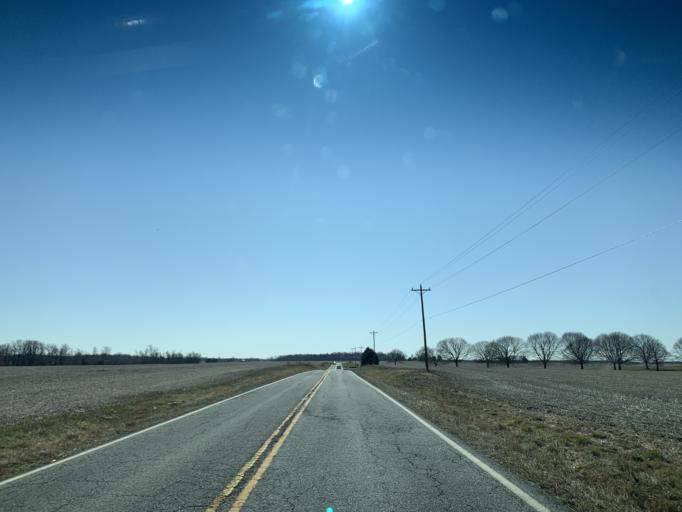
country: US
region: Maryland
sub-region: Cecil County
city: Charlestown
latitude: 39.4468
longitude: -75.9018
